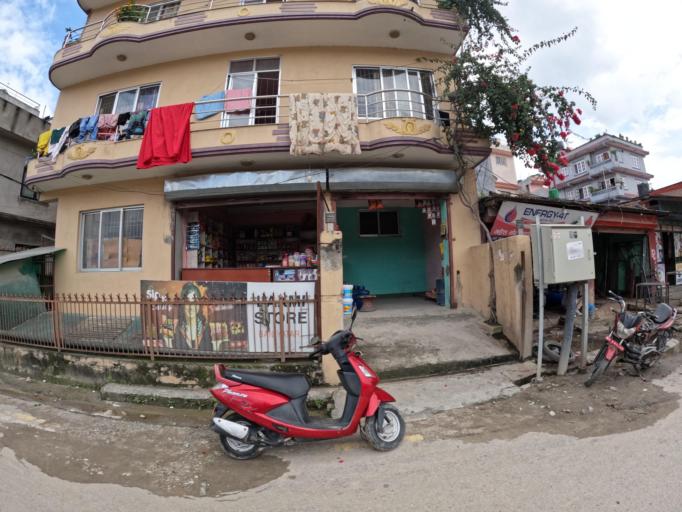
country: NP
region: Central Region
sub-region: Bagmati Zone
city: Kathmandu
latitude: 27.7479
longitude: 85.3152
